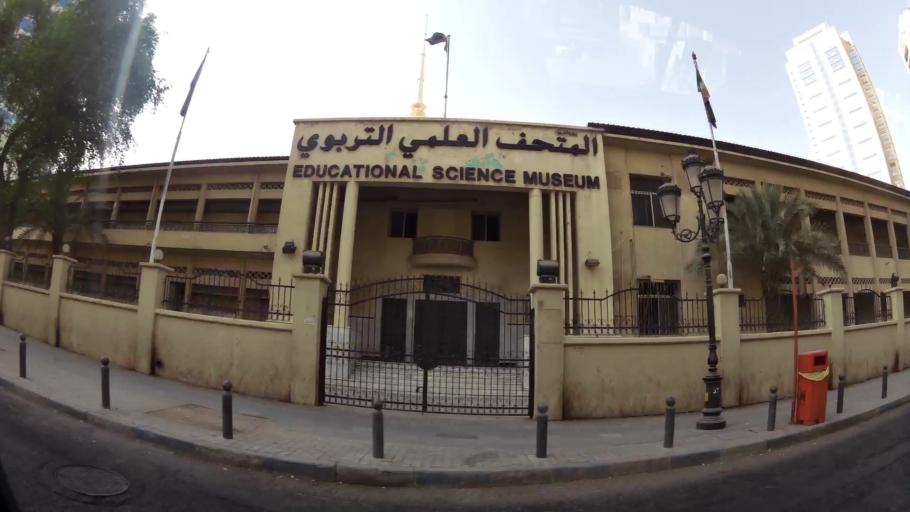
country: KW
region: Al Asimah
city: Kuwait City
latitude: 29.3711
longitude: 47.9773
